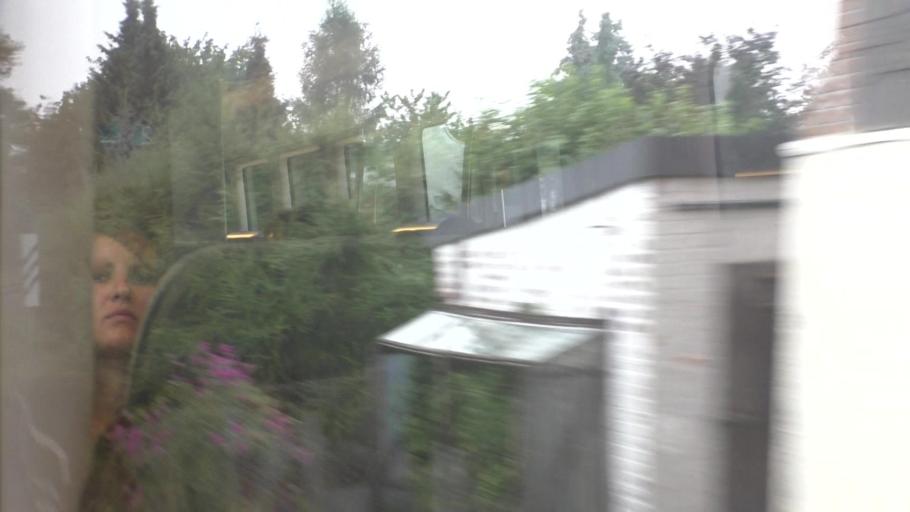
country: DE
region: Saxony
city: Neugersdorf
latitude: 50.9884
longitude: 14.5932
